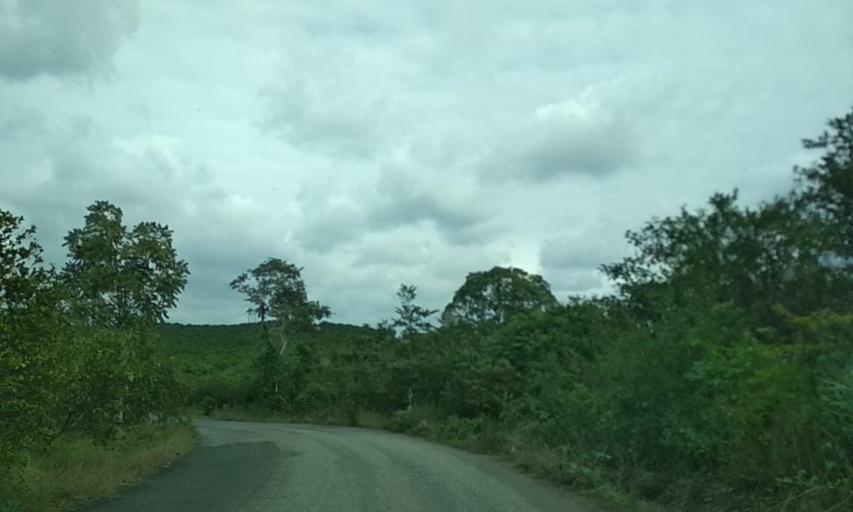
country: MX
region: Veracruz
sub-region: Papantla
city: El Chote
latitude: 20.3532
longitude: -97.3695
